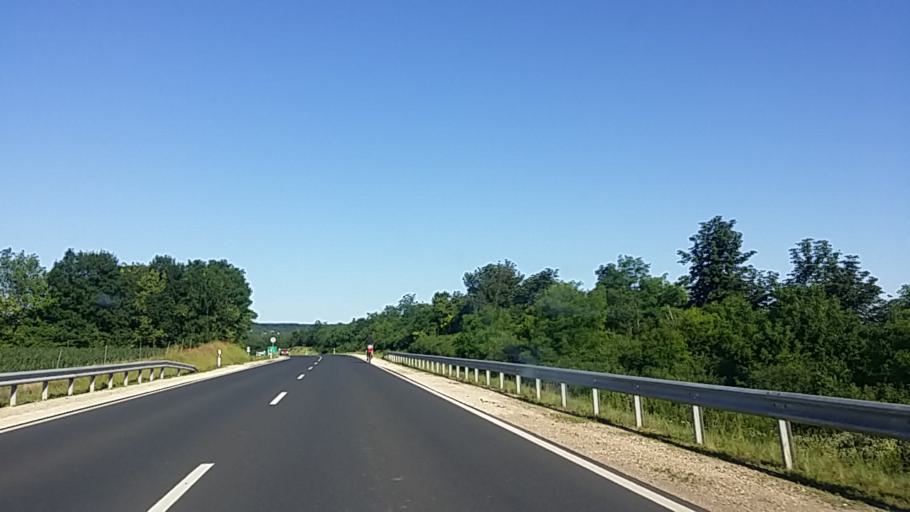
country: HU
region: Zala
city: Heviz
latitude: 46.7611
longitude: 17.1983
